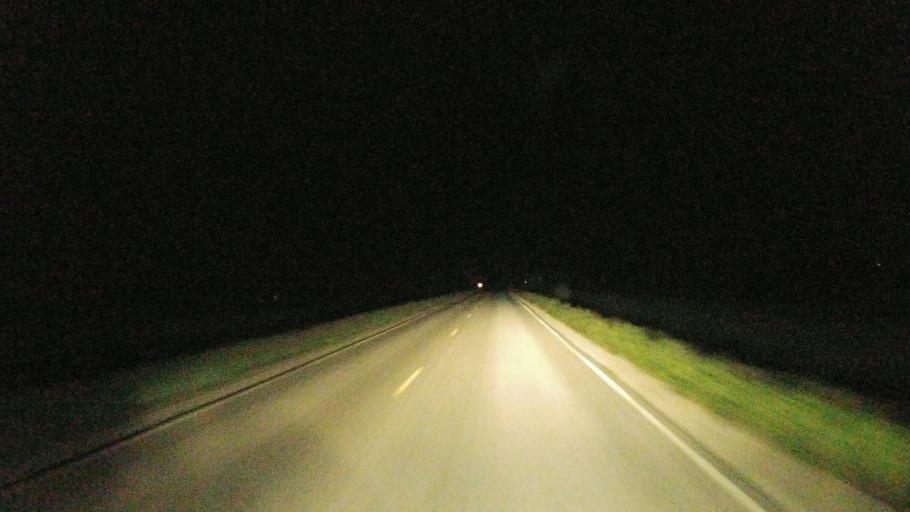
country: US
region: Iowa
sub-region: Decatur County
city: Lamoni
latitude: 40.6238
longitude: -93.9681
